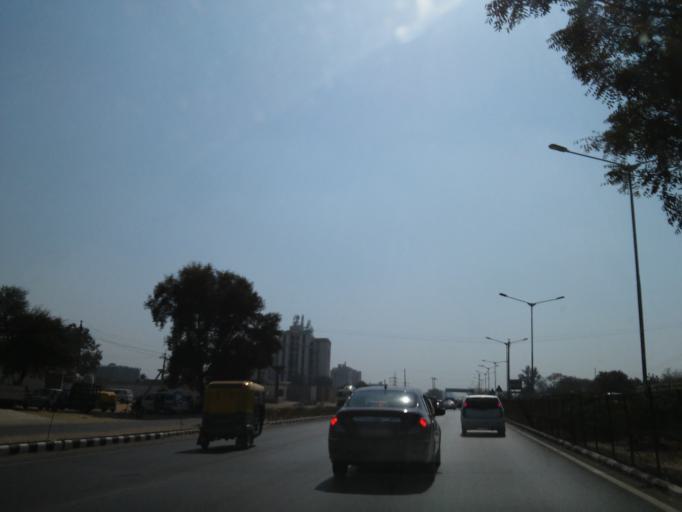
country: IN
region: Gujarat
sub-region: Gandhinagar
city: Adalaj
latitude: 23.1090
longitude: 72.5348
